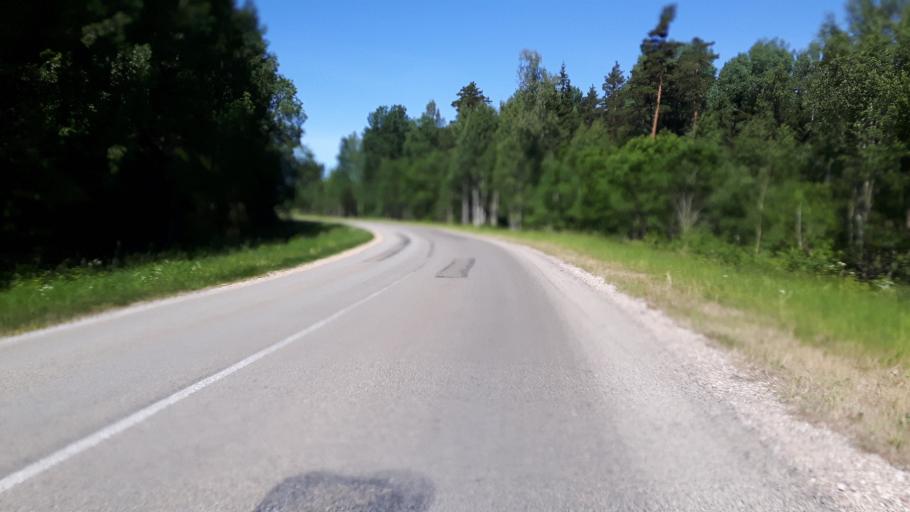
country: LV
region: Tukuma Rajons
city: Tukums
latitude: 57.0161
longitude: 23.0443
